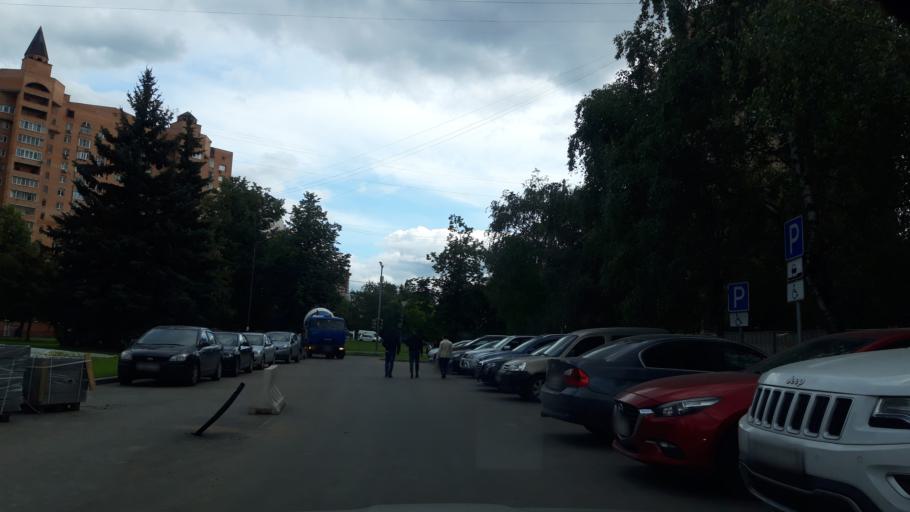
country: RU
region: Moskovskaya
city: Levoberezhnyy
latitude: 55.8511
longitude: 37.4789
